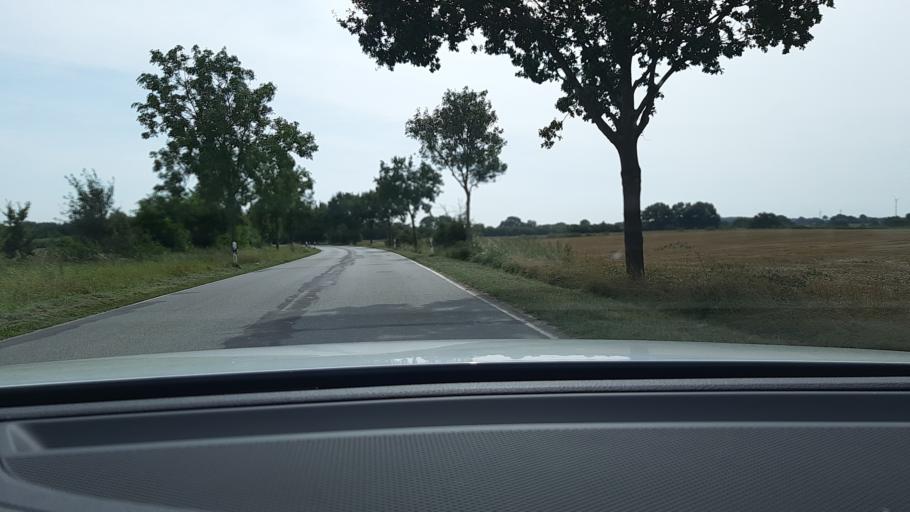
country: DE
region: Schleswig-Holstein
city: Heilshoop
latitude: 53.8973
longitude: 10.5239
